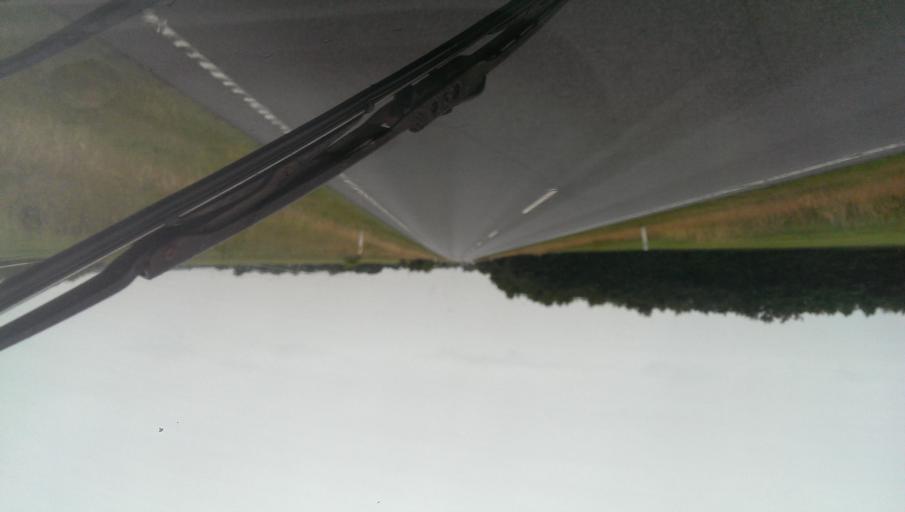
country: DK
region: South Denmark
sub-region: Esbjerg Kommune
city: Esbjerg
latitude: 55.5321
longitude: 8.4273
